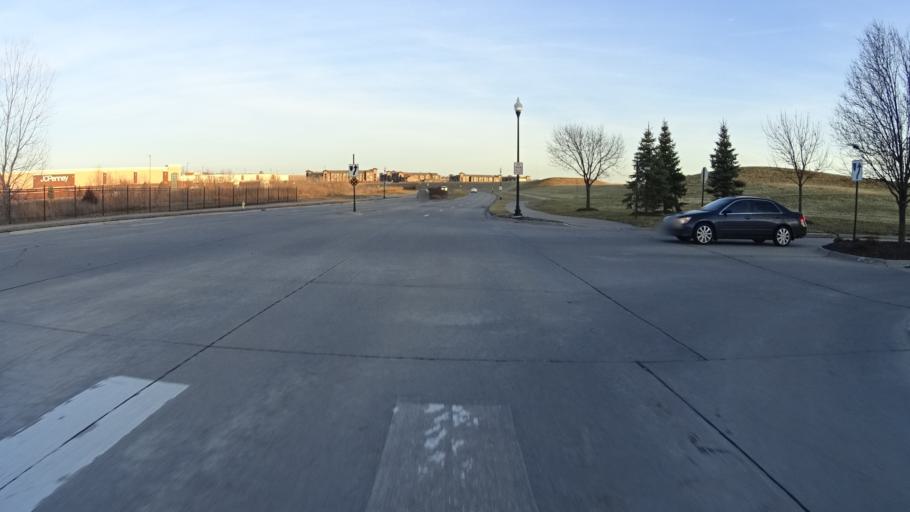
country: US
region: Nebraska
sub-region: Sarpy County
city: Papillion
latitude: 41.1327
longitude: -96.0340
